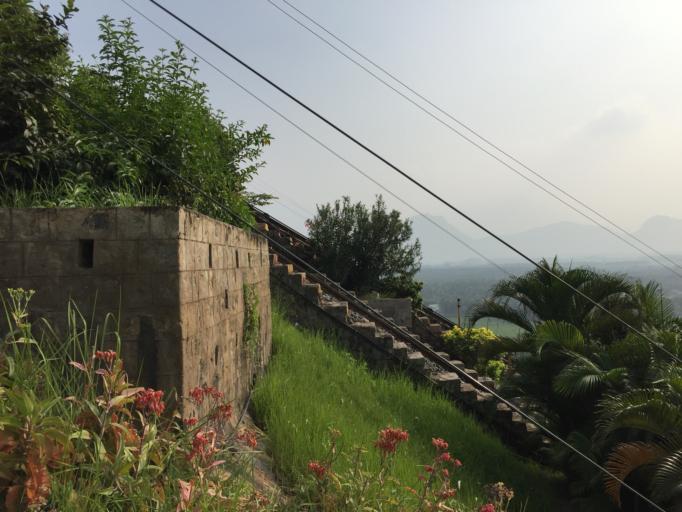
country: IN
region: Tamil Nadu
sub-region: Dindigul
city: Palani
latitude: 10.4385
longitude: 77.5179
